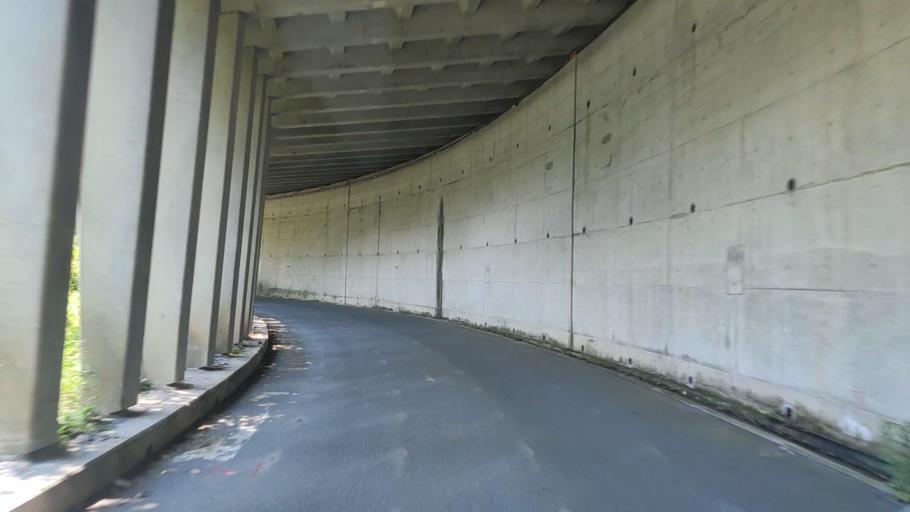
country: JP
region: Gifu
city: Godo
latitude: 35.6931
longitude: 136.5822
